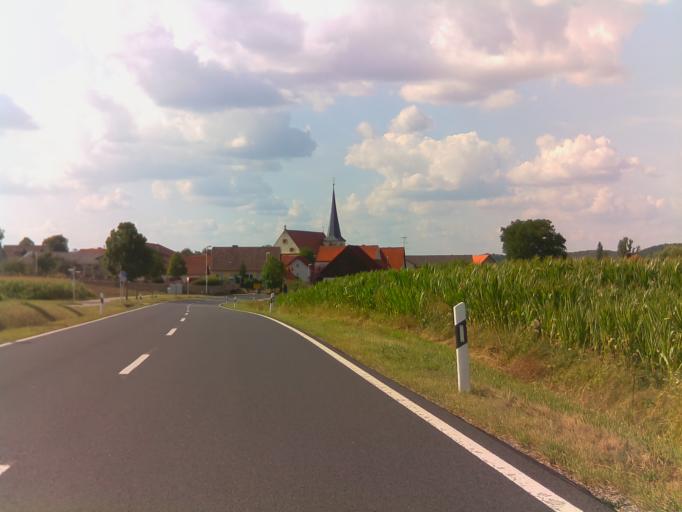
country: DE
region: Bavaria
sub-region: Regierungsbezirk Unterfranken
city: Bundorf
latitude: 50.2693
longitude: 10.5289
